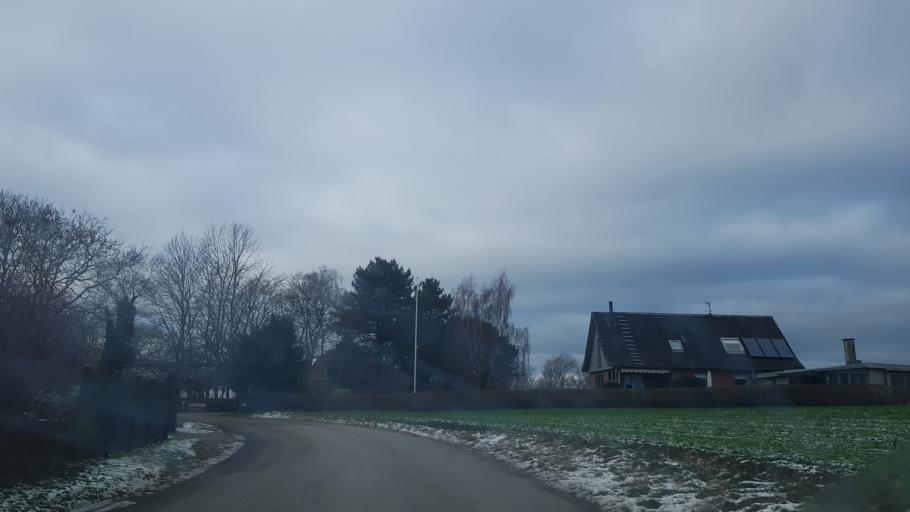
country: DK
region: Zealand
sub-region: Odsherred Kommune
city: Hojby
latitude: 55.9273
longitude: 11.5566
